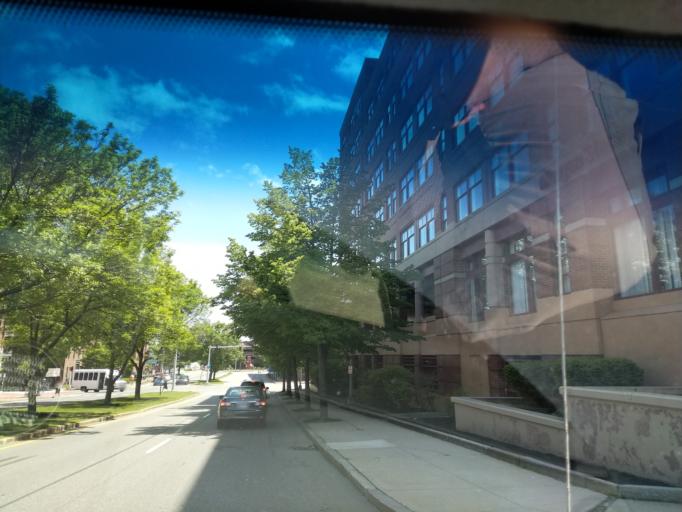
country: US
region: Maine
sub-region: Cumberland County
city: Portland
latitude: 43.6592
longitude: -70.2517
